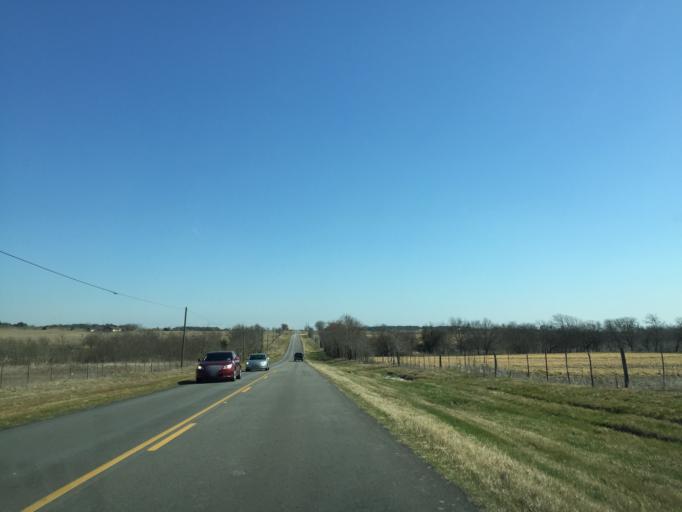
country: US
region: Texas
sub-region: Williamson County
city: Serenada
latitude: 30.7342
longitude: -97.6089
